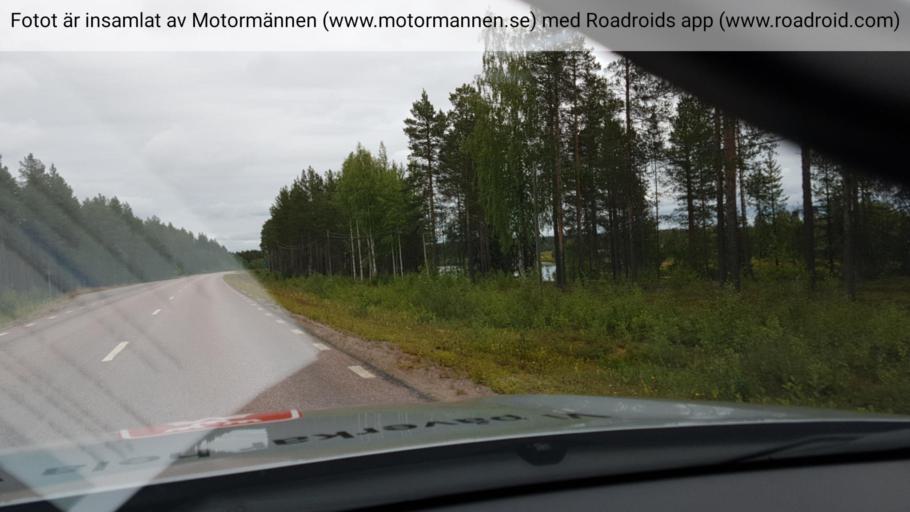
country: SE
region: Norrbotten
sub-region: Overkalix Kommun
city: OEverkalix
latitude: 67.0740
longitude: 22.5268
